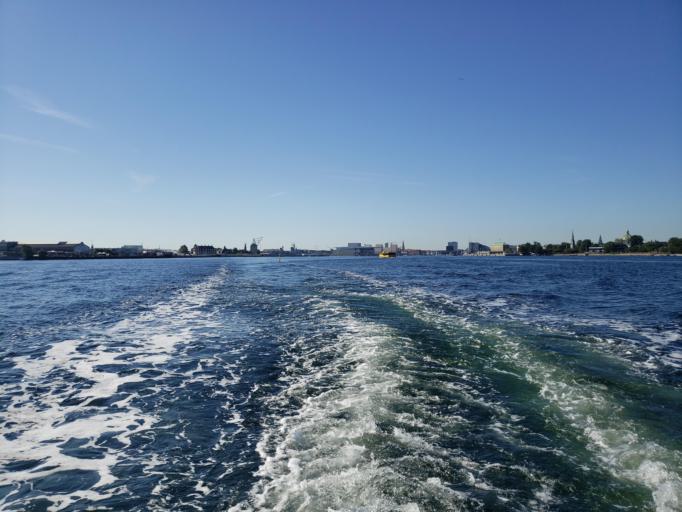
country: DK
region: Capital Region
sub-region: Kobenhavn
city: Christianshavn
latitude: 55.6973
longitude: 12.6056
